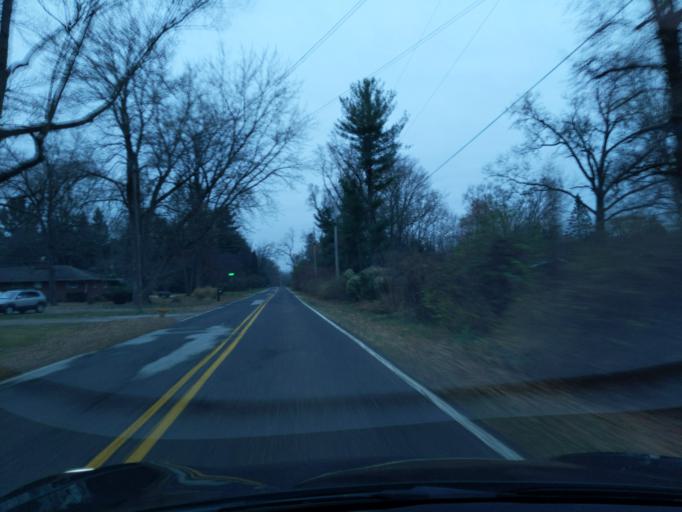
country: US
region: Indiana
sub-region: Saint Joseph County
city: Georgetown
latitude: 41.7280
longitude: -86.2555
